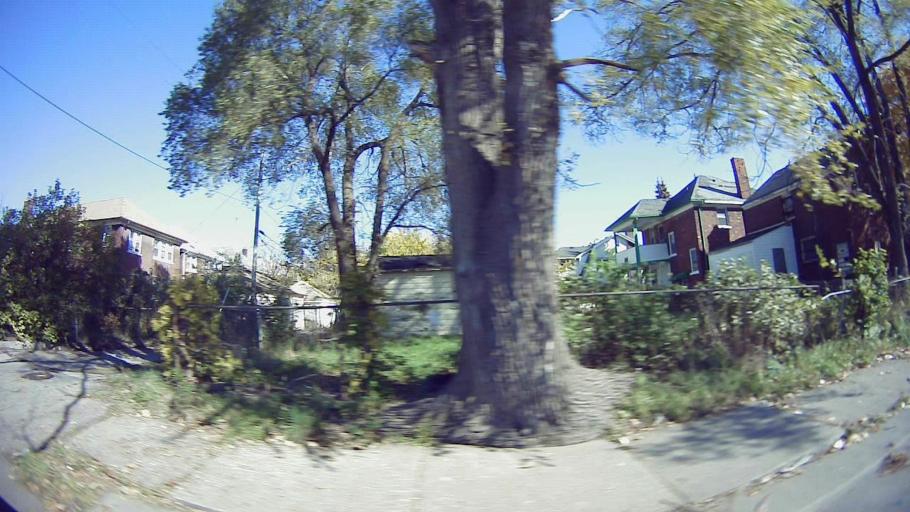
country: US
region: Michigan
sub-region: Wayne County
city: Highland Park
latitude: 42.3792
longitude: -83.1124
